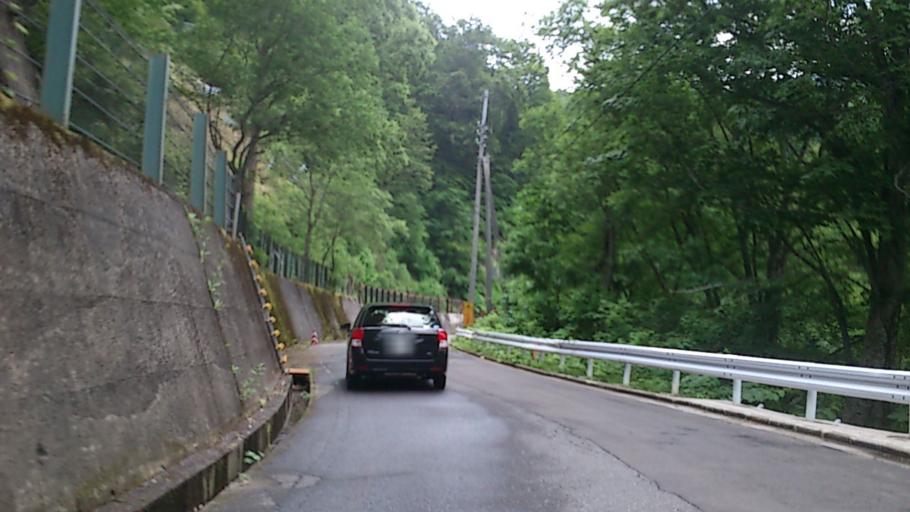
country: JP
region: Aomori
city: Hirosaki
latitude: 40.5170
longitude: 140.1809
